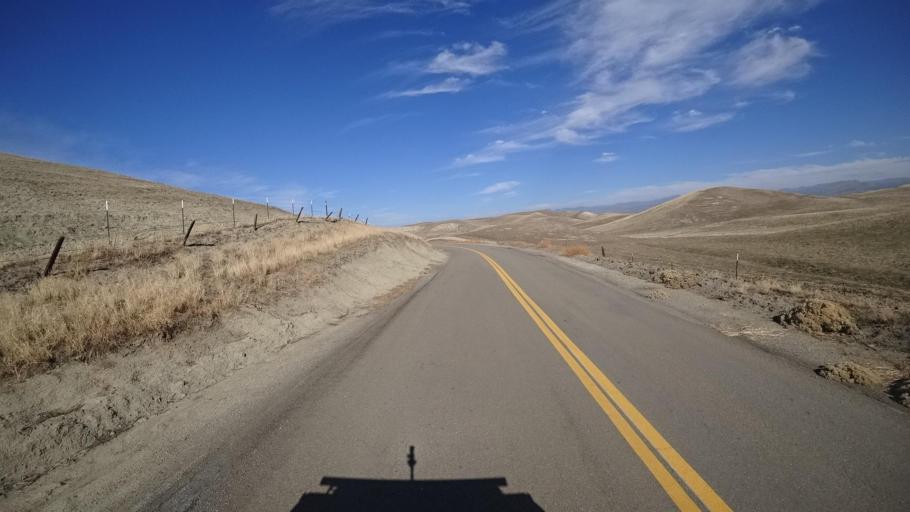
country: US
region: California
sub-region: Kern County
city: Oildale
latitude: 35.6197
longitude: -118.9416
